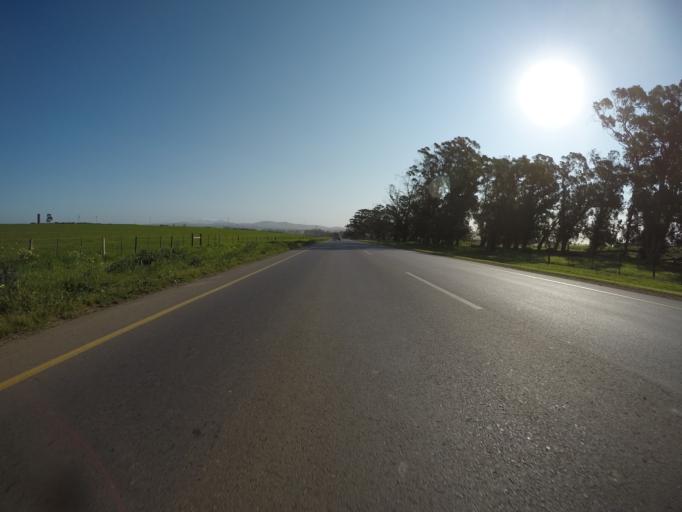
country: ZA
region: Western Cape
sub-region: City of Cape Town
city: Kraaifontein
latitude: -33.7767
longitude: 18.7350
